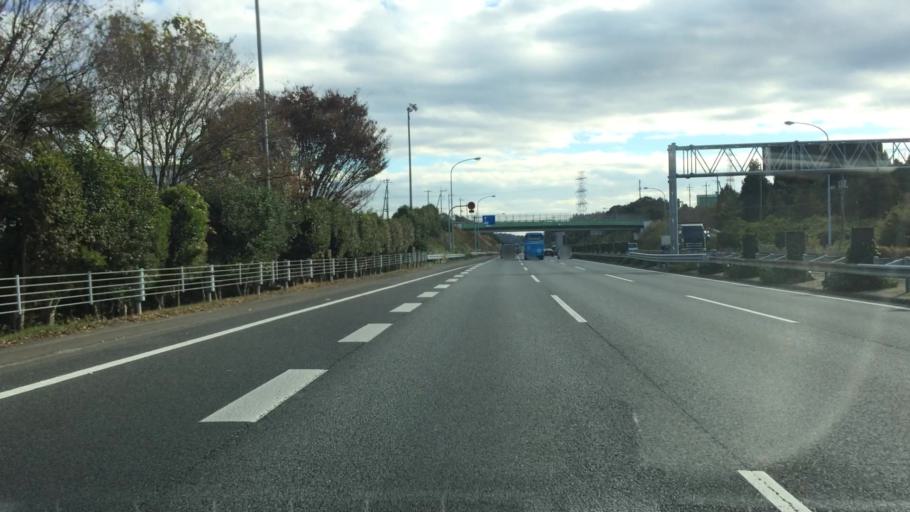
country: JP
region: Chiba
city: Yotsukaido
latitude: 35.6842
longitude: 140.1850
